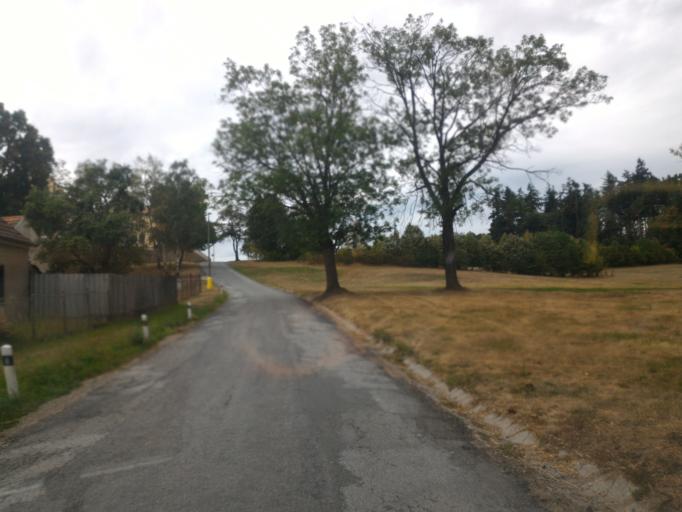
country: CZ
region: Jihocesky
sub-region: Okres Jindrichuv Hradec
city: Dacice
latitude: 49.1045
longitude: 15.4196
